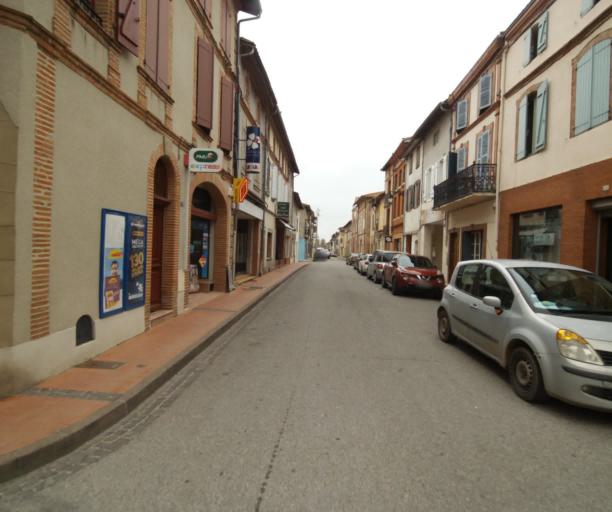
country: FR
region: Midi-Pyrenees
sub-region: Departement de l'Ariege
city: Mazeres
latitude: 43.2513
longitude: 1.6787
